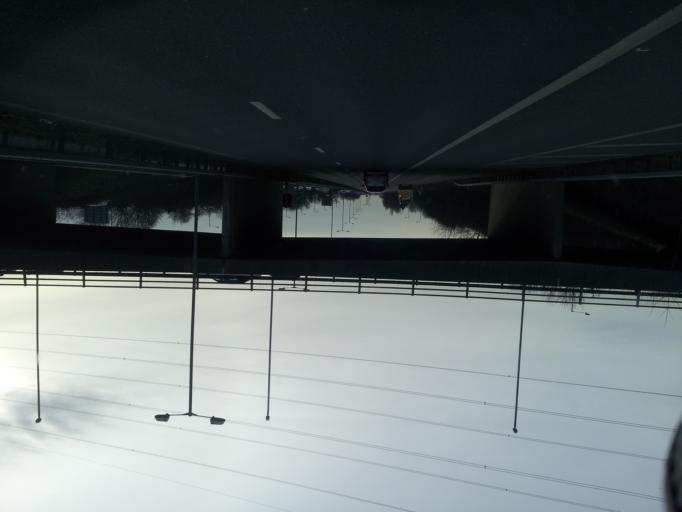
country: GB
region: England
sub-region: Greater London
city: High Barnet
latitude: 51.6846
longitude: -0.2306
